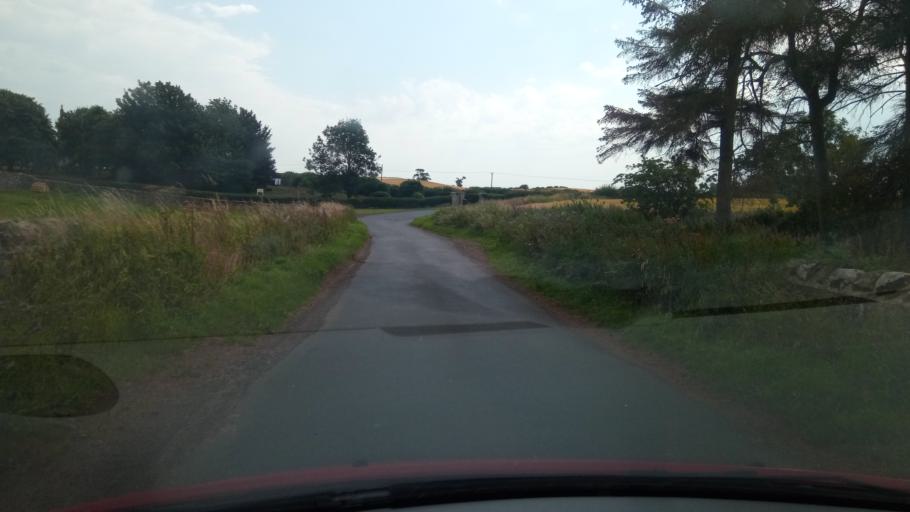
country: GB
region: Scotland
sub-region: The Scottish Borders
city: Kelso
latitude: 55.5898
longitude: -2.4702
